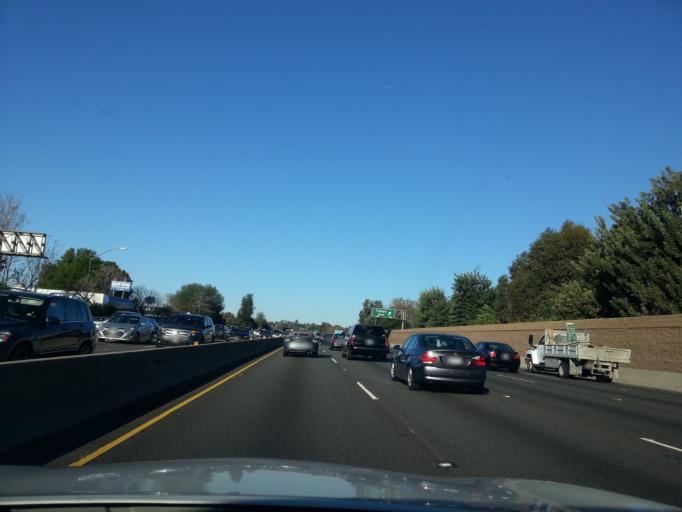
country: US
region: California
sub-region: Los Angeles County
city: Northridge
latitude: 34.1735
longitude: -118.5483
